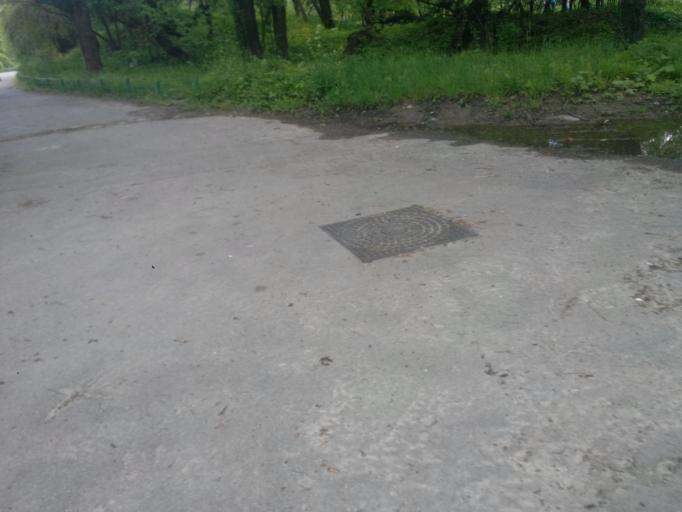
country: RO
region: Bucuresti
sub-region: Municipiul Bucuresti
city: Bucuresti
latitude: 44.4391
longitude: 26.0636
